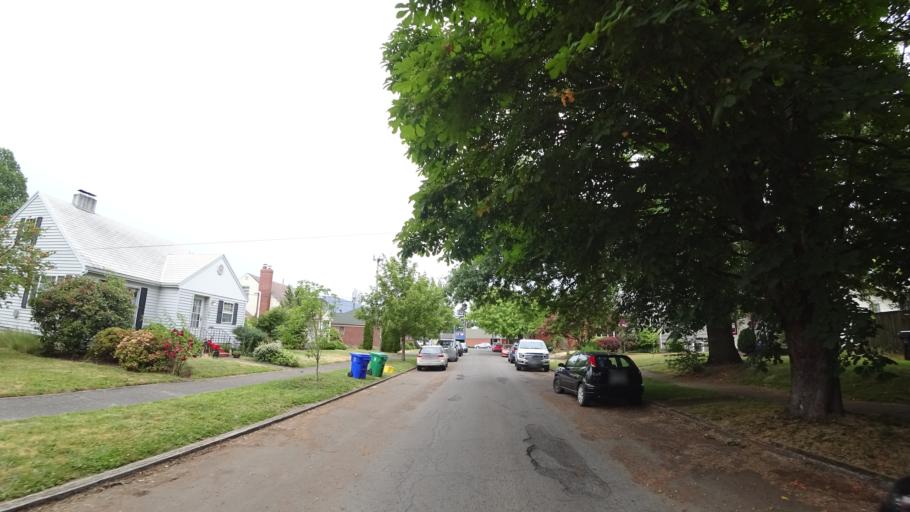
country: US
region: Oregon
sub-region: Multnomah County
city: Portland
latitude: 45.5763
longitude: -122.7016
